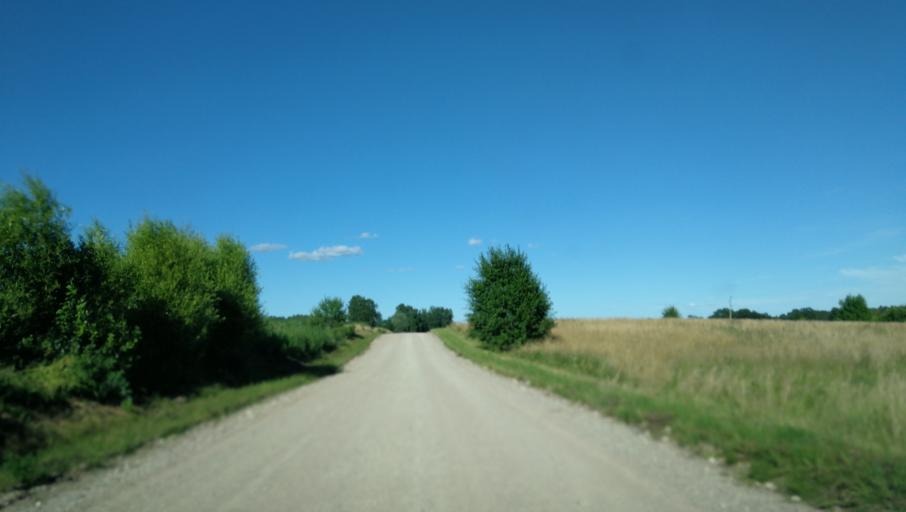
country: LV
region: Jaunpiebalga
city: Jaunpiebalga
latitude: 57.0117
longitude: 26.0467
